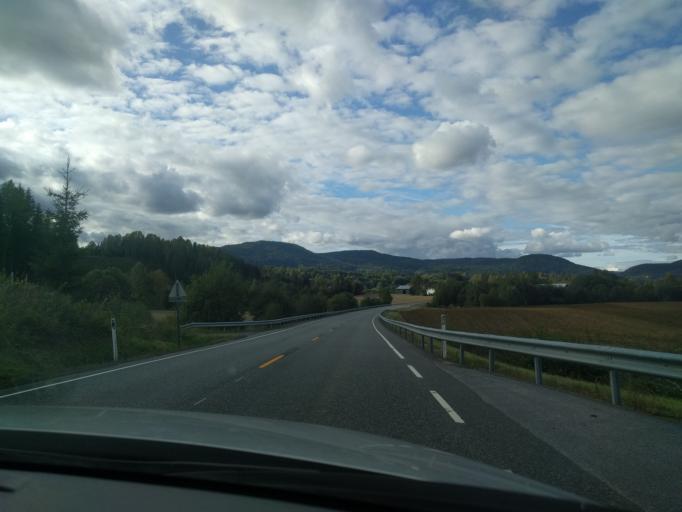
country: NO
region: Vestfold
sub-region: Lardal
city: Svarstad
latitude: 59.2920
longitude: 9.8947
